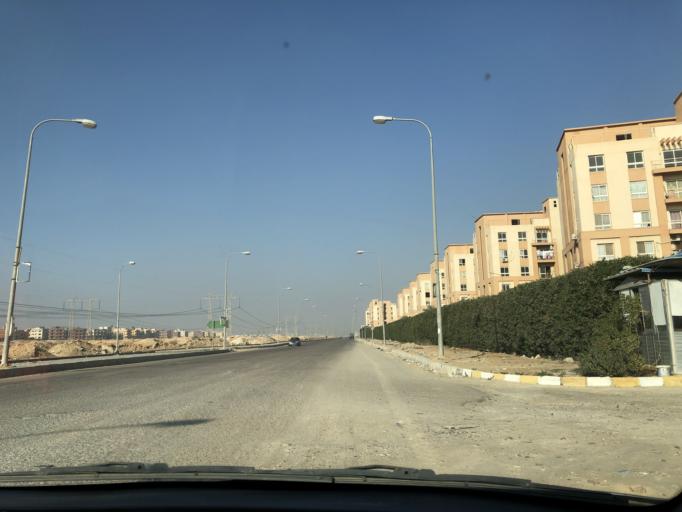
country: EG
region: Al Jizah
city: Madinat Sittah Uktubar
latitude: 29.9115
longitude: 31.0522
